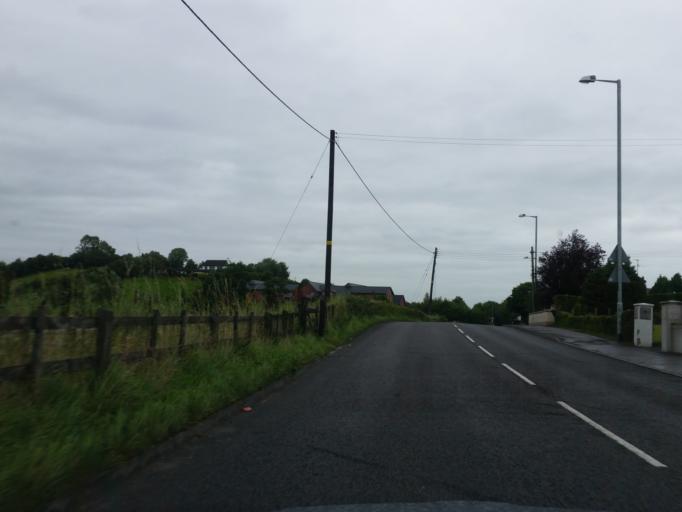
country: GB
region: Northern Ireland
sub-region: Fermanagh District
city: Enniskillen
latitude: 54.3380
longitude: -7.6484
